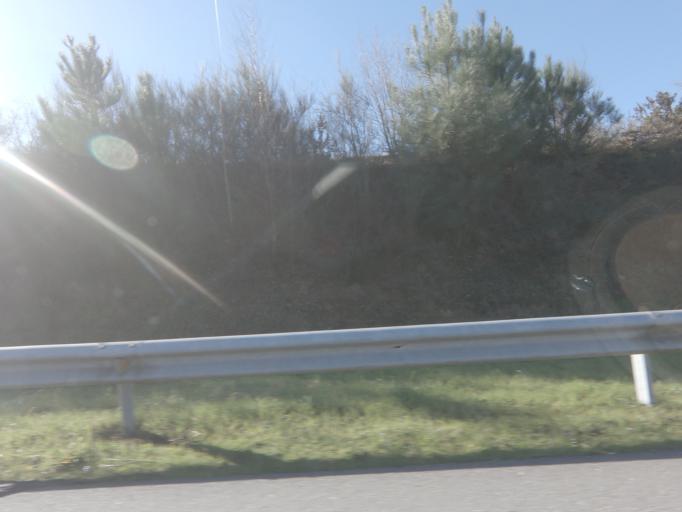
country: ES
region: Galicia
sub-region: Provincia de Pontevedra
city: Lalin
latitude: 42.6741
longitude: -8.1627
